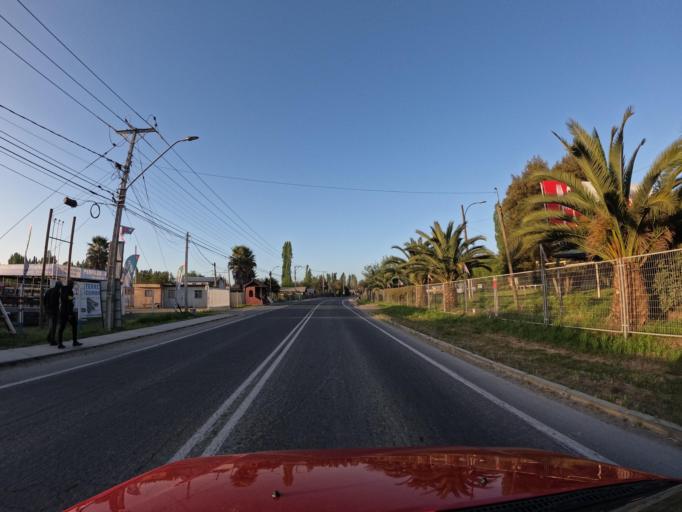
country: CL
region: O'Higgins
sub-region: Provincia de Cachapoal
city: San Vicente
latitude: -34.1841
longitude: -71.4017
